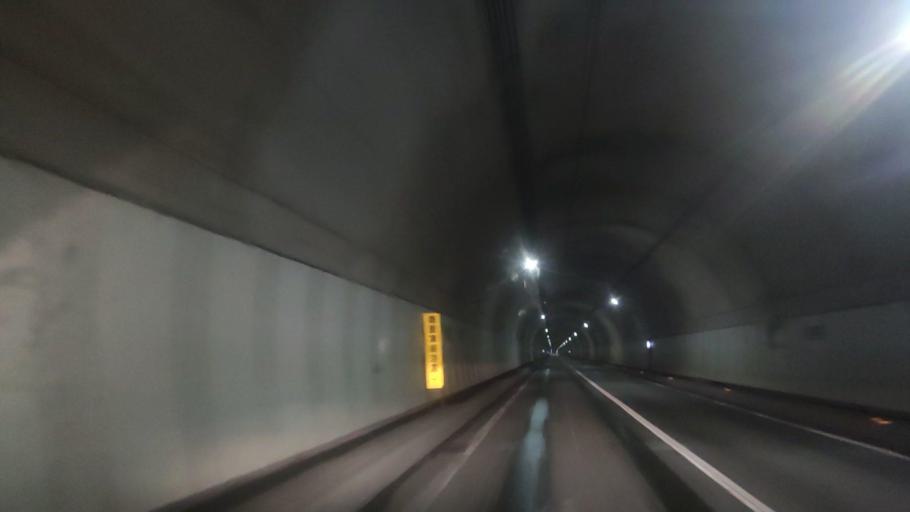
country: JP
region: Hokkaido
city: Date
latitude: 42.5541
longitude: 141.0741
